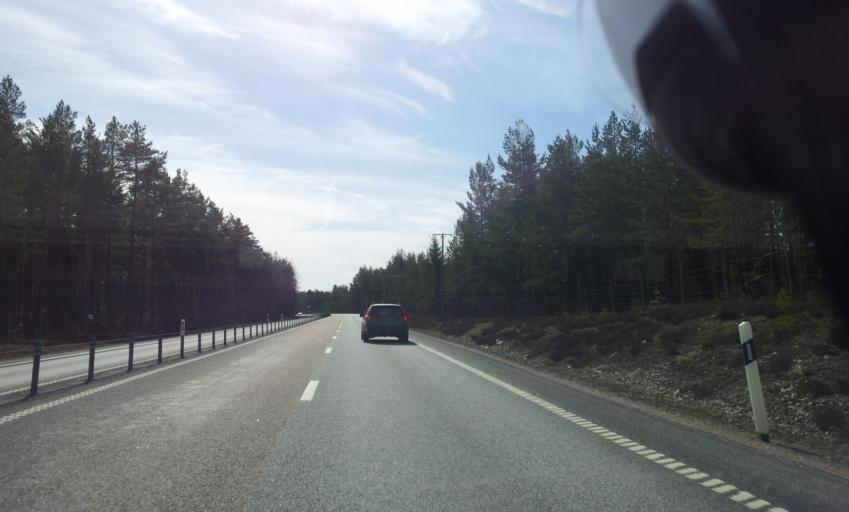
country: SE
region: Gaevleborg
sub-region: Gavle Kommun
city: Norrsundet
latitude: 61.0228
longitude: 16.9763
